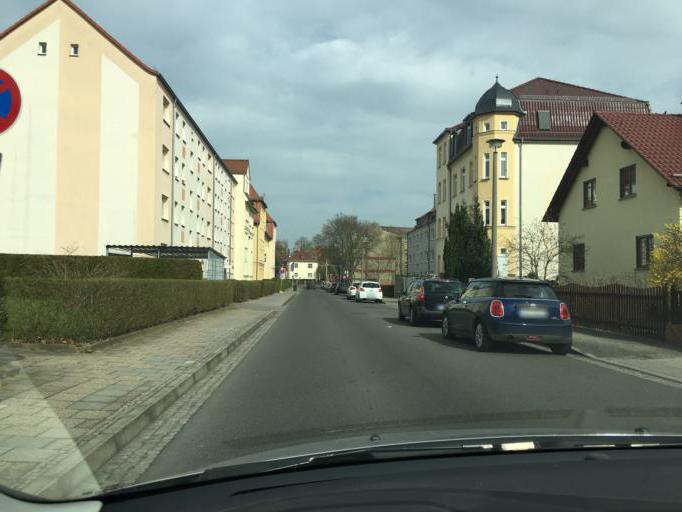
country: DE
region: Saxony
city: Taucha
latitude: 51.3771
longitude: 12.4917
